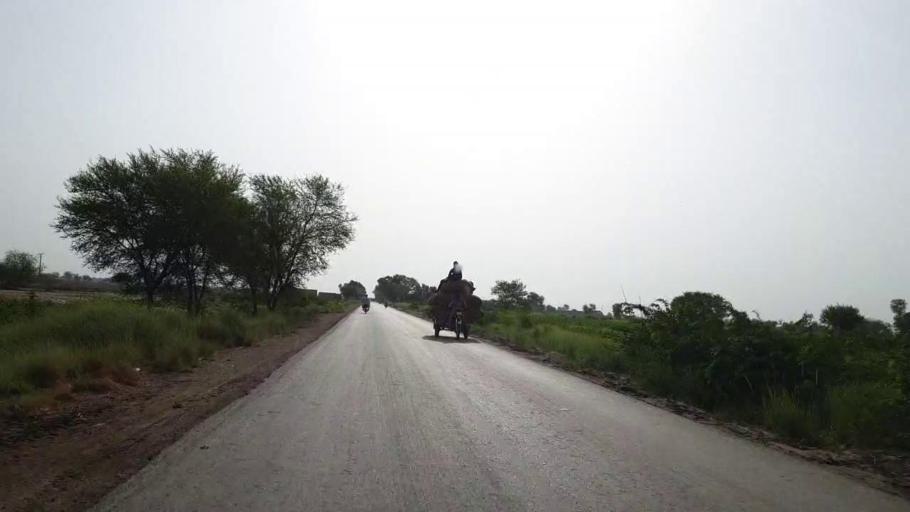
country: PK
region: Sindh
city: Nawabshah
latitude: 26.2606
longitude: 68.4866
